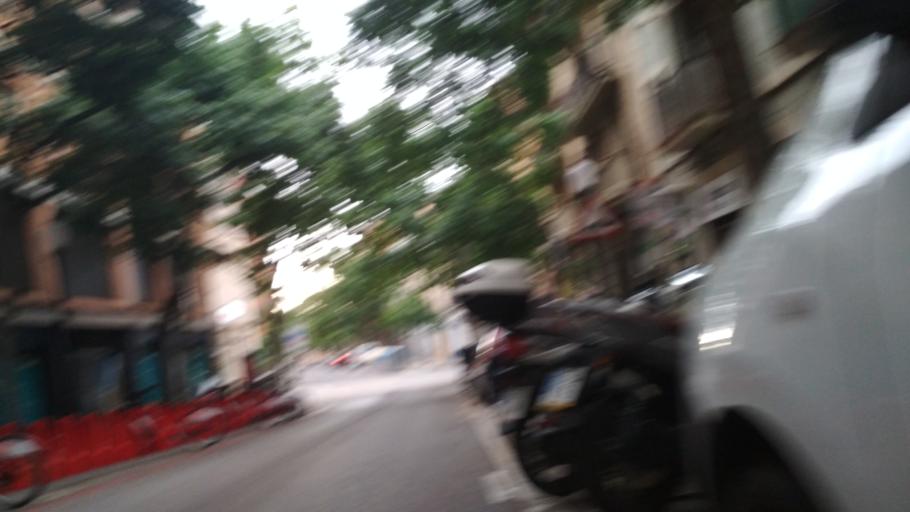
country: ES
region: Catalonia
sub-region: Provincia de Barcelona
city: Sant Andreu de Palomar
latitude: 41.4361
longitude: 2.1891
